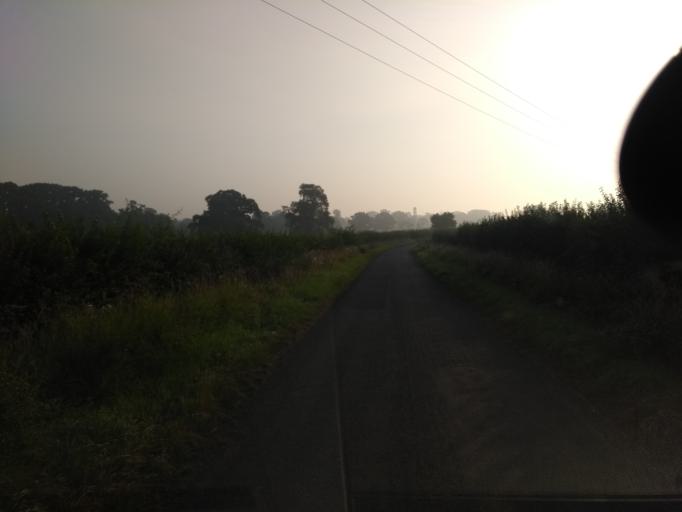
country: GB
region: England
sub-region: Somerset
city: Curry Rivel
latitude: 50.9857
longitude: -2.8767
